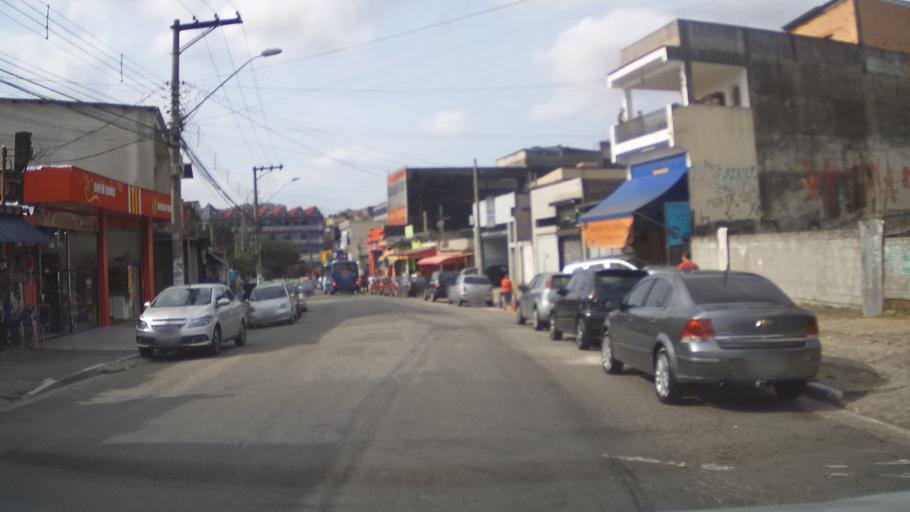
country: BR
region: Sao Paulo
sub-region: Guarulhos
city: Guarulhos
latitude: -23.4072
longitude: -46.4542
